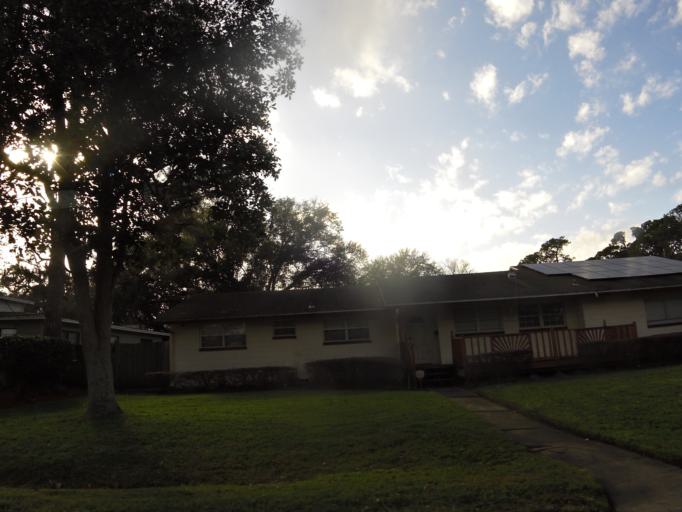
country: US
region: Florida
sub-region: Duval County
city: Jacksonville
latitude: 30.2796
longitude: -81.6114
